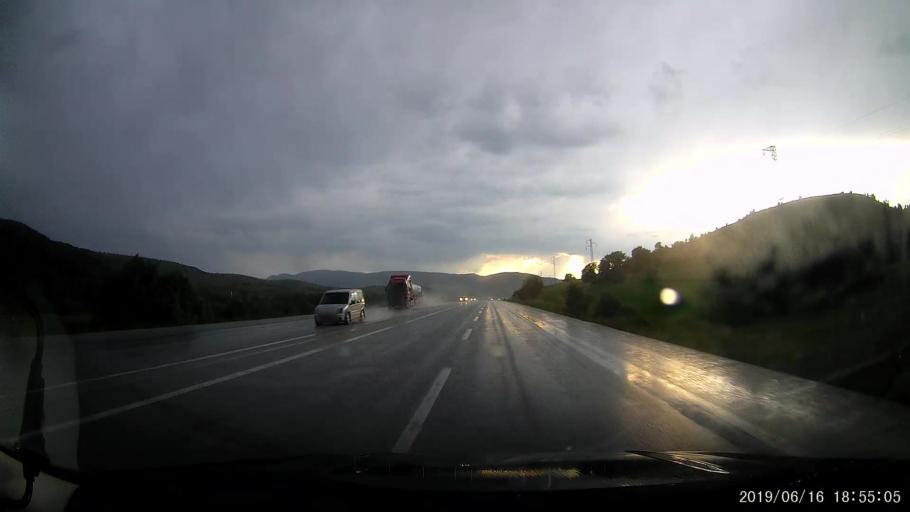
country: TR
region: Erzincan
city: Refahiye
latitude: 39.8988
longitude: 38.8370
